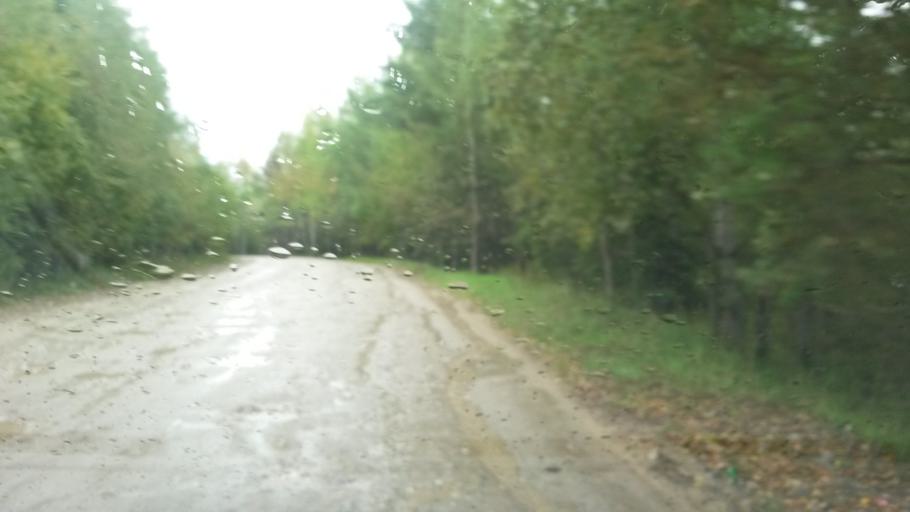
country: RU
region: Ivanovo
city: Zarechnyy
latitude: 57.5033
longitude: 42.2883
